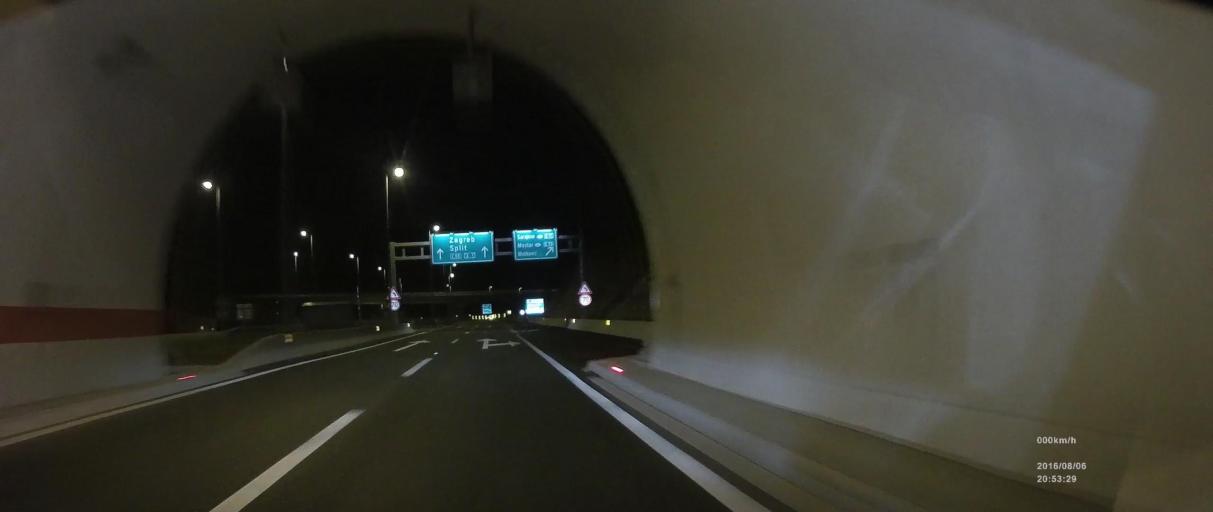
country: BA
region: Federation of Bosnia and Herzegovina
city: Ljubuski
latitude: 43.1436
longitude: 17.4882
